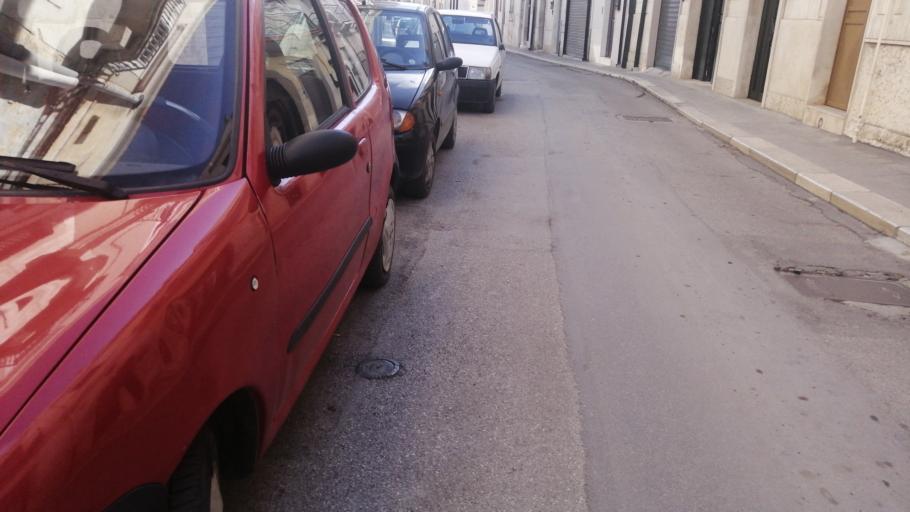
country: IT
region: Apulia
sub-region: Provincia di Barletta - Andria - Trani
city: Andria
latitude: 41.2225
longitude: 16.2940
